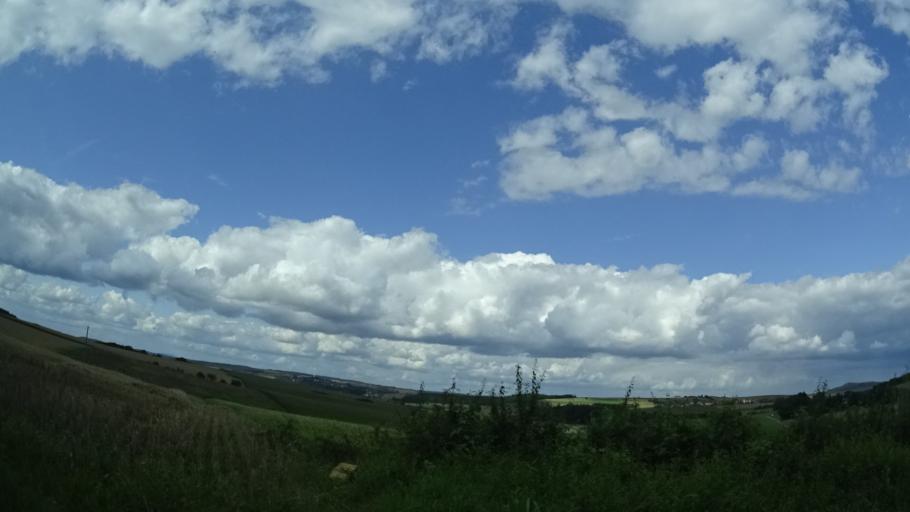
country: DE
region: Bavaria
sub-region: Upper Franconia
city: Ebensfeld
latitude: 50.1094
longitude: 10.9206
